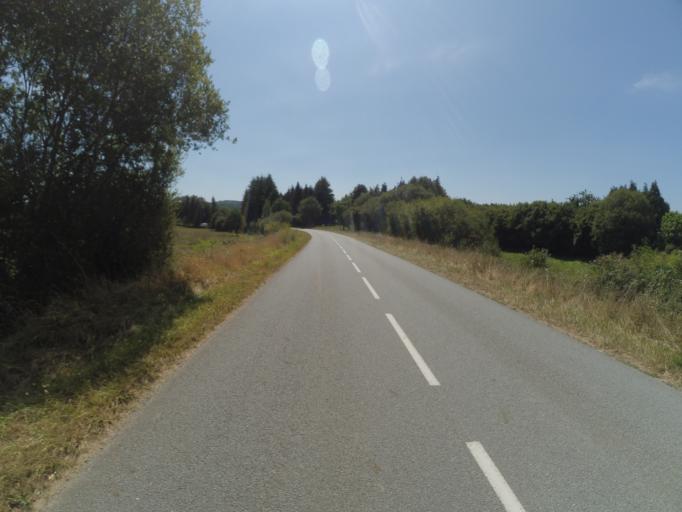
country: FR
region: Limousin
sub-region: Departement de la Creuse
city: Le Grand-Bourg
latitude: 46.0995
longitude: 1.6769
